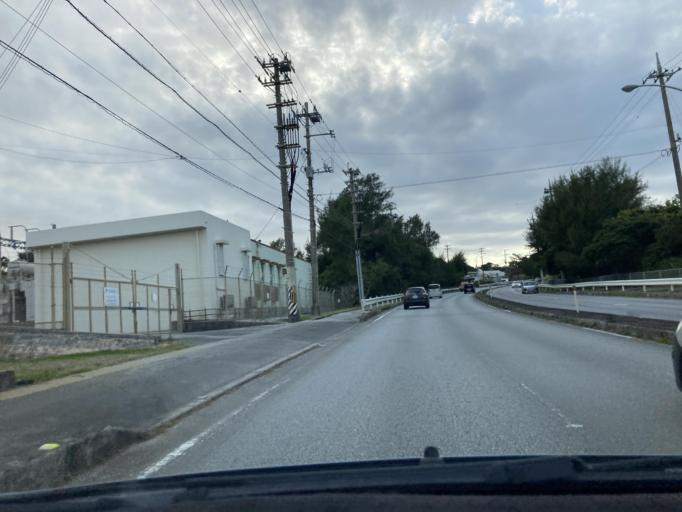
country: JP
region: Okinawa
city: Ishikawa
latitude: 26.4334
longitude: 127.8158
